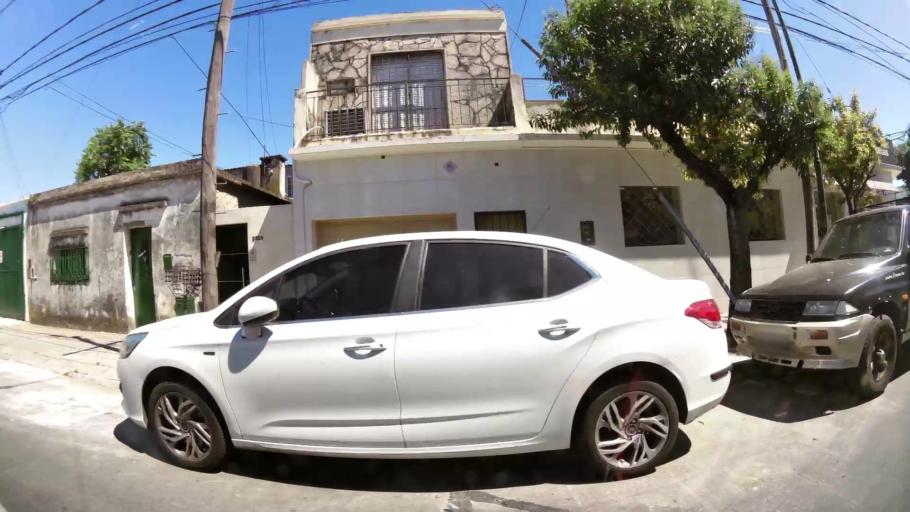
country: AR
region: Buenos Aires
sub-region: Partido de General San Martin
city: General San Martin
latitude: -34.5267
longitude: -58.5517
